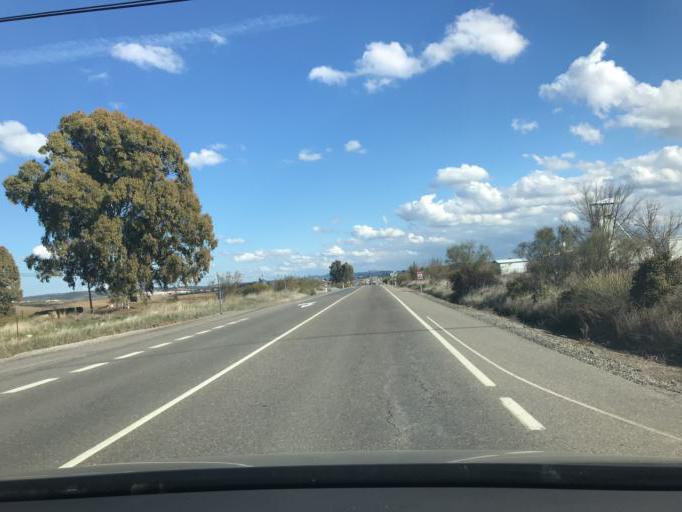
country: ES
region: Andalusia
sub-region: Province of Cordoba
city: Penarroya-Pueblonuevo
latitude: 38.3004
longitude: -5.3156
